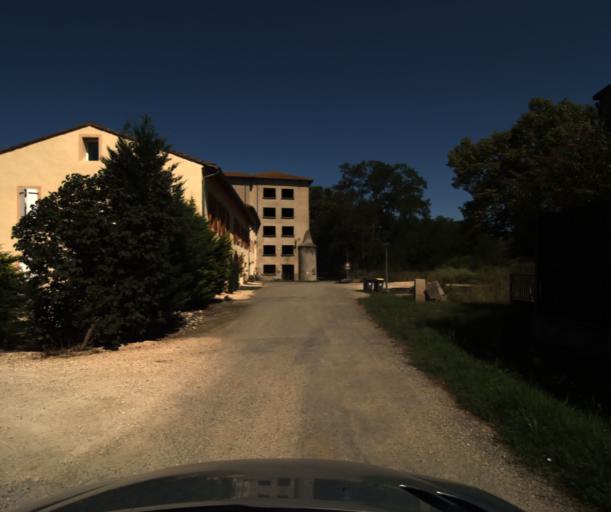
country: FR
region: Midi-Pyrenees
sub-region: Departement de la Haute-Garonne
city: Roquettes
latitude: 43.5026
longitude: 1.3698
